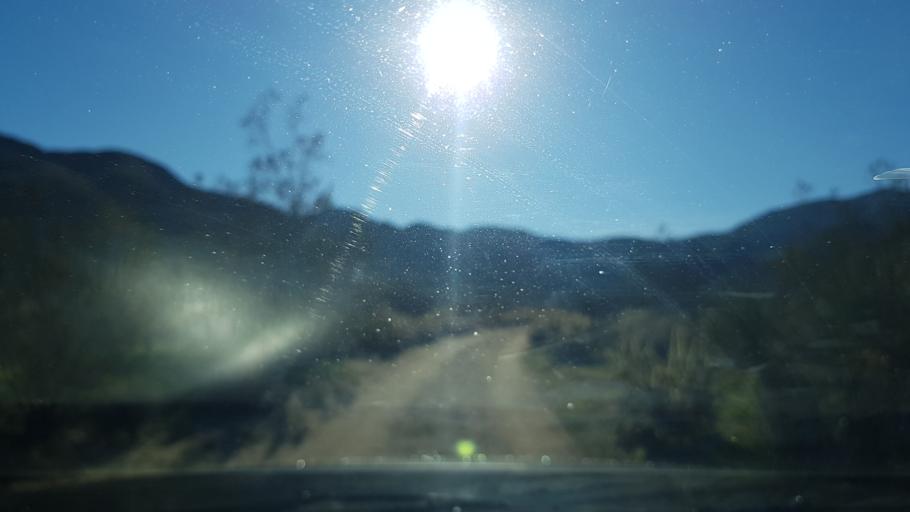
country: US
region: California
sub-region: San Diego County
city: Julian
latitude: 33.0516
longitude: -116.4250
